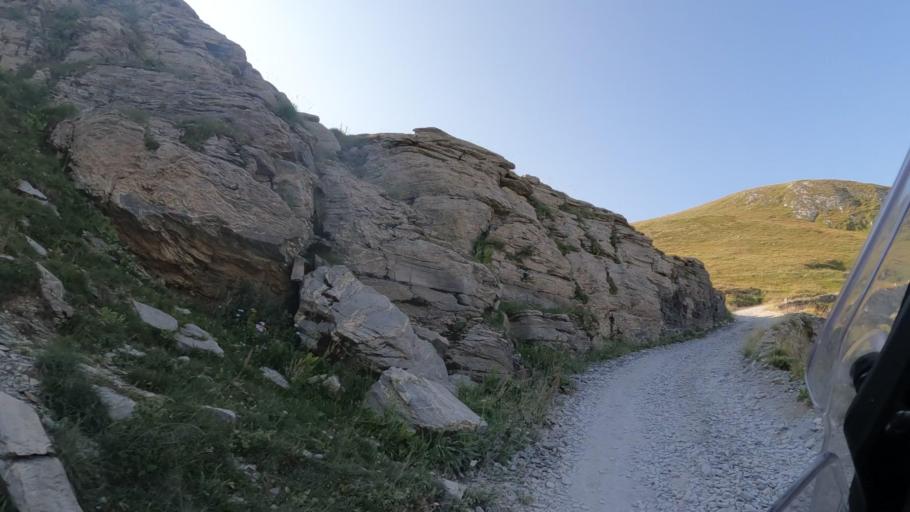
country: IT
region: Piedmont
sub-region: Provincia di Cuneo
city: Limone Piemonte
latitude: 44.1708
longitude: 7.6479
